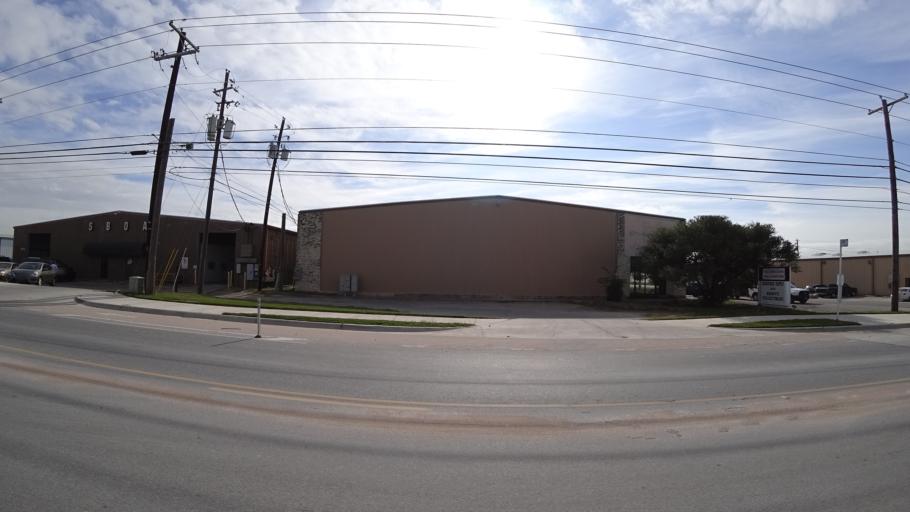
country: US
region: Texas
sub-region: Travis County
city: Austin
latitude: 30.2091
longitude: -97.7391
